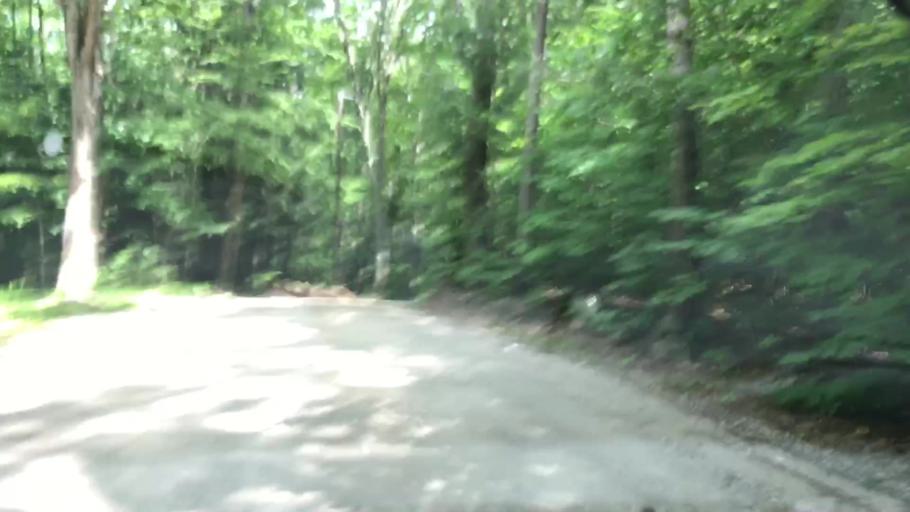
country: US
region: New Hampshire
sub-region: Hillsborough County
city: Mont Vernon
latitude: 42.8854
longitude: -71.6169
